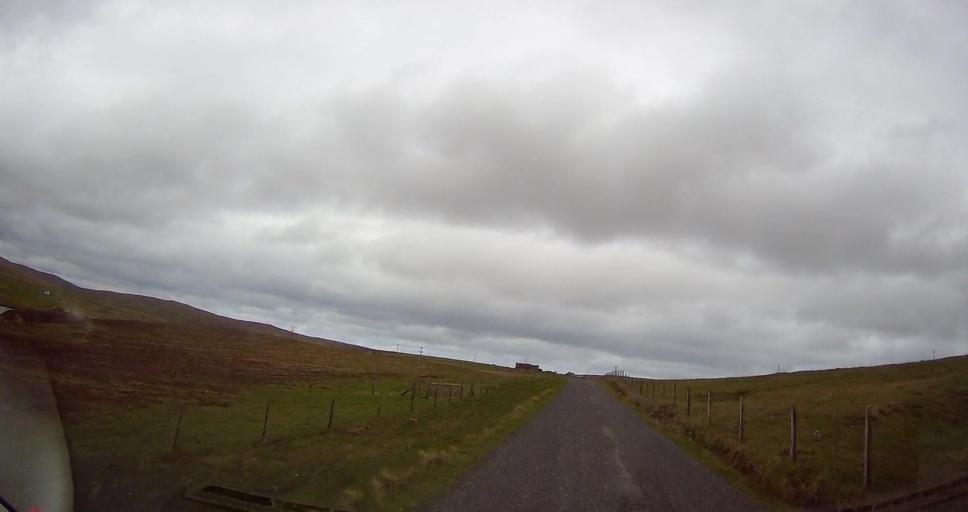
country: GB
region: Scotland
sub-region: Shetland Islands
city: Shetland
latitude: 60.7986
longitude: -0.8647
